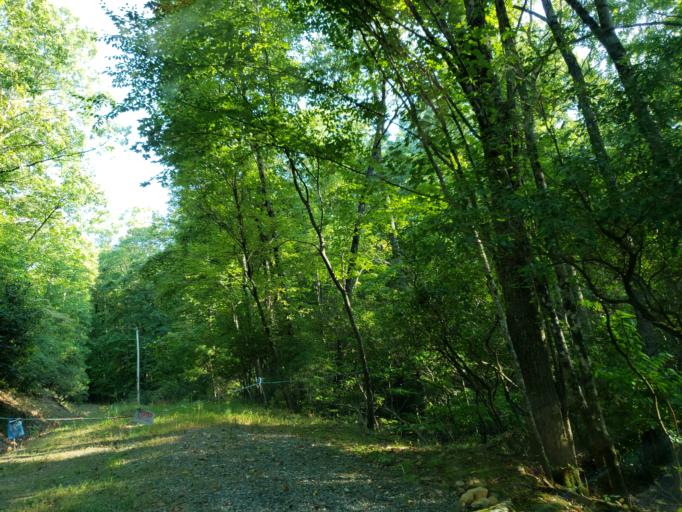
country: US
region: Georgia
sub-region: Fannin County
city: Blue Ridge
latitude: 34.6813
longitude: -84.2583
